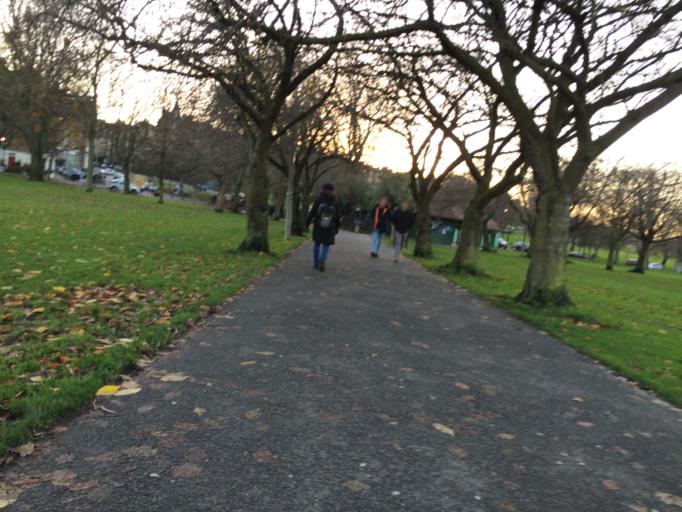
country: GB
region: Scotland
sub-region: Edinburgh
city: Edinburgh
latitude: 55.9411
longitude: -3.1939
